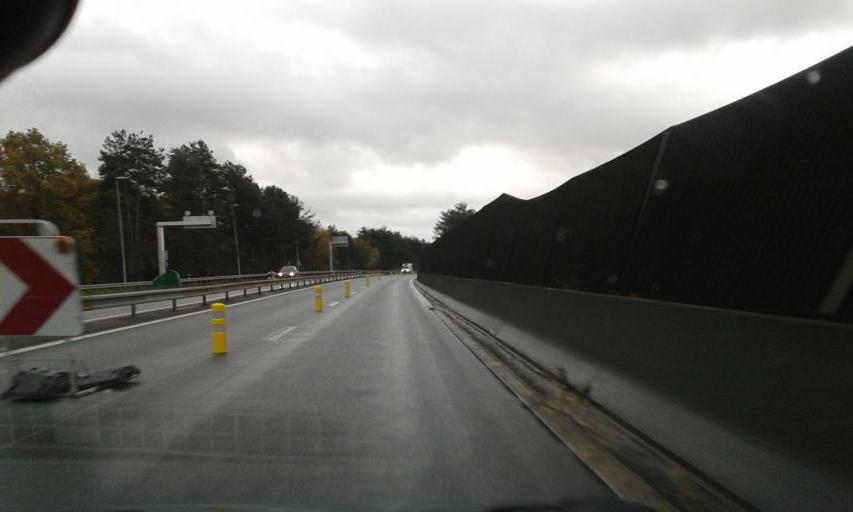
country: FR
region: Centre
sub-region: Departement du Loiret
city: Saran
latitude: 47.9481
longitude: 1.8685
